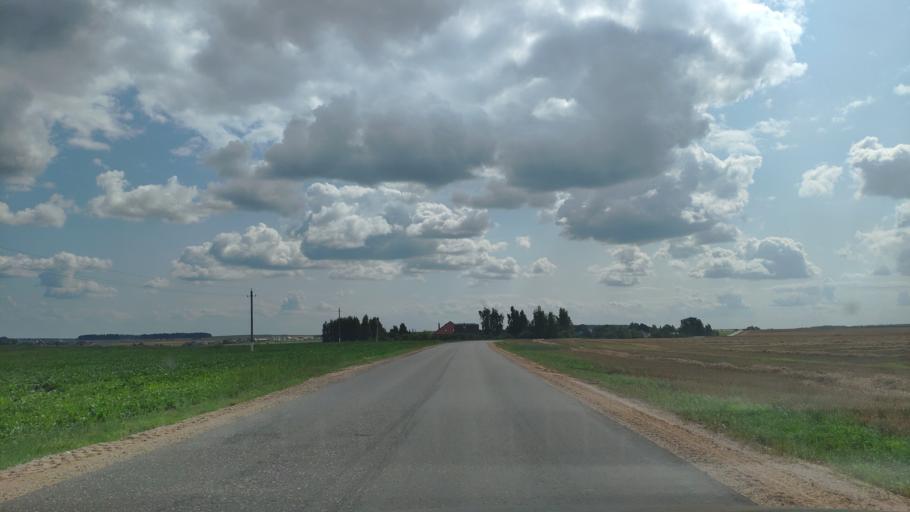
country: BY
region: Minsk
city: Khatsyezhyna
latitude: 53.8437
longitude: 27.3133
